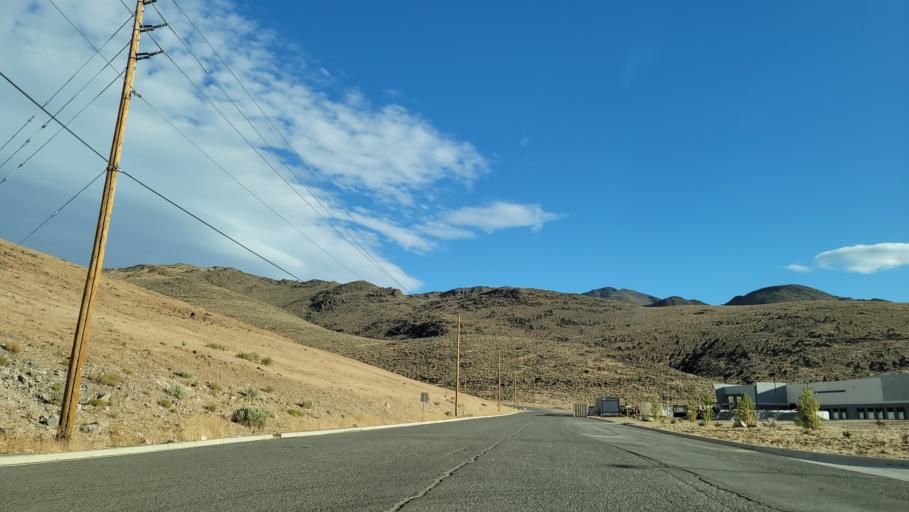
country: US
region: Nevada
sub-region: Washoe County
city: Spanish Springs
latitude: 39.5566
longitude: -119.5260
